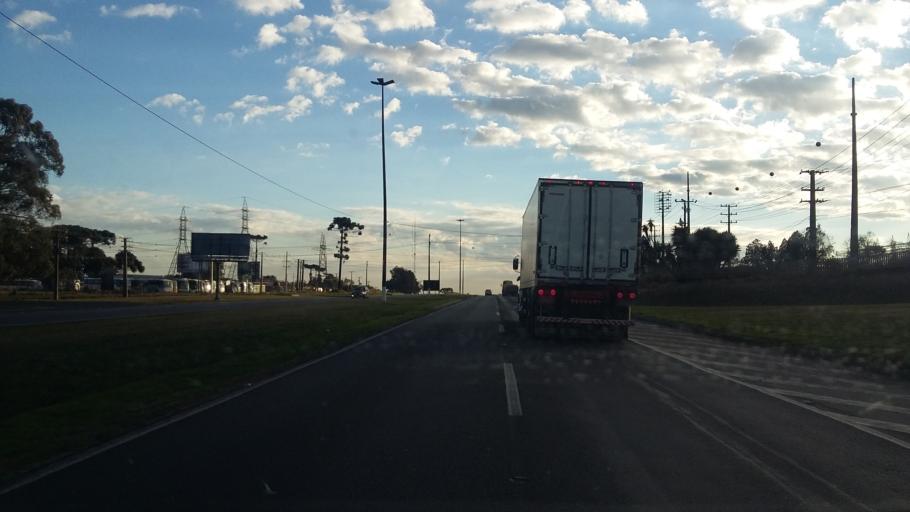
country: BR
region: Parana
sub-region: Curitiba
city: Curitiba
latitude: -25.4320
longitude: -49.3664
